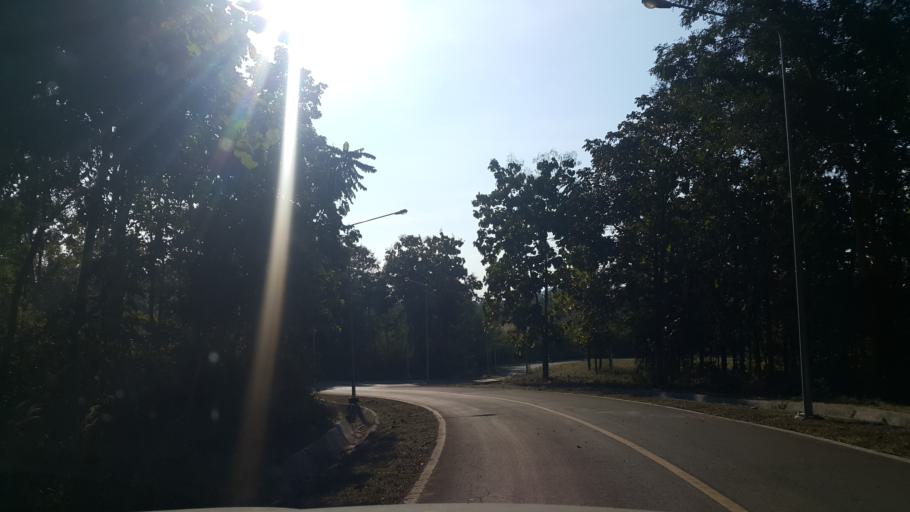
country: TH
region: Lamphun
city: Mae Tha
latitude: 18.5114
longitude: 99.1124
